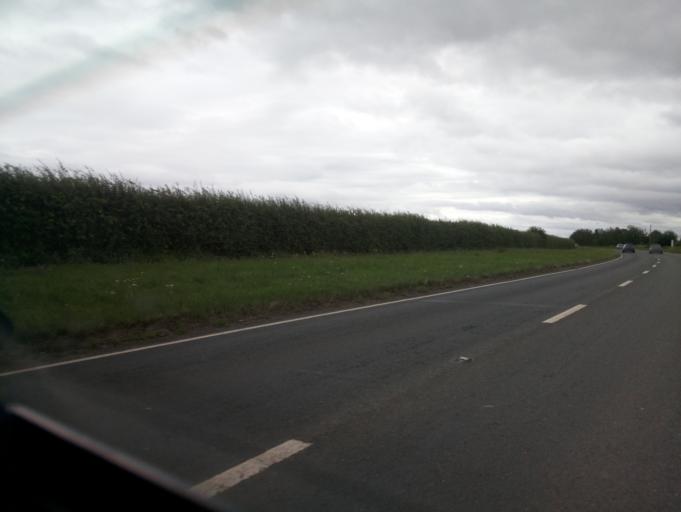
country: GB
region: England
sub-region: Worcestershire
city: Kempsey
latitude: 52.1520
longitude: -2.2166
